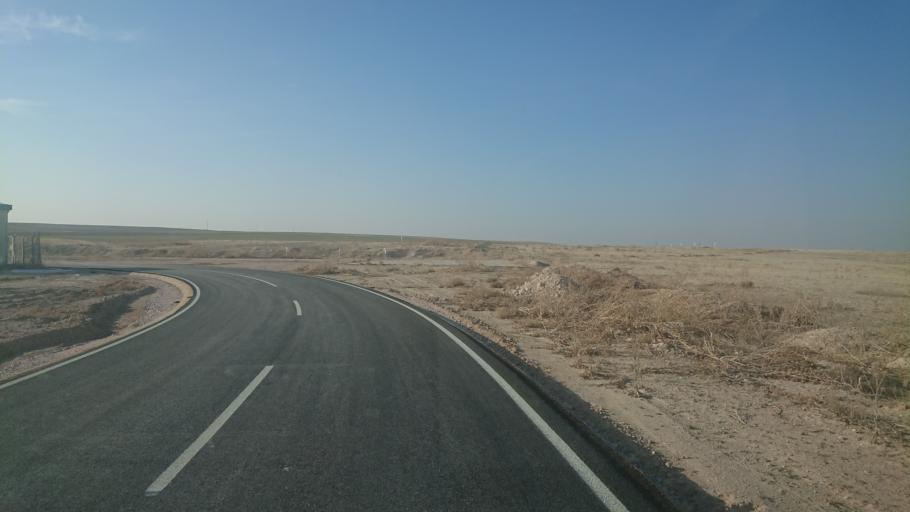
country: TR
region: Aksaray
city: Sultanhani
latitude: 38.0841
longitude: 33.6116
